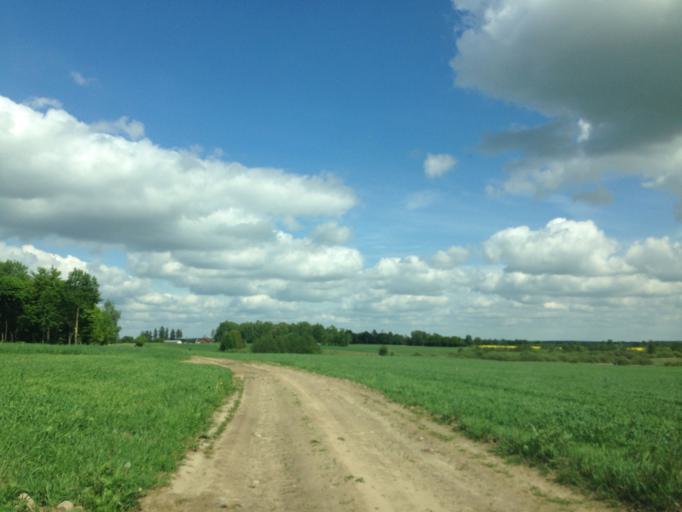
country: PL
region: Warmian-Masurian Voivodeship
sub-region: Powiat ostrodzki
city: Dabrowno
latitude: 53.3945
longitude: 20.1473
